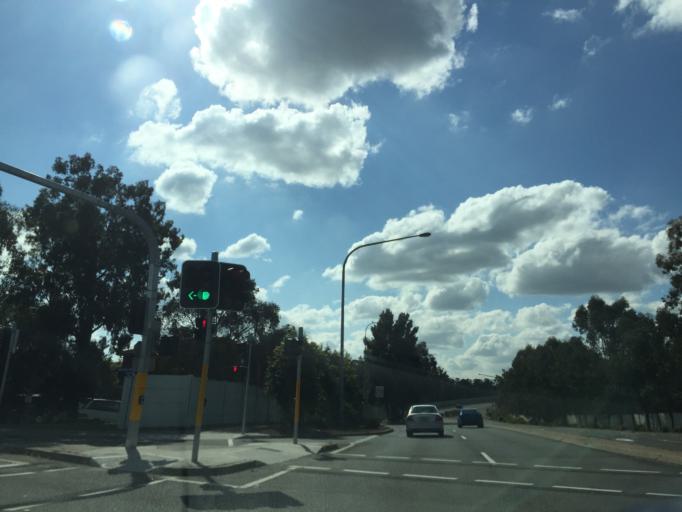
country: AU
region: New South Wales
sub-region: Blacktown
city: Quakers Hill
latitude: -33.7281
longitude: 150.8810
